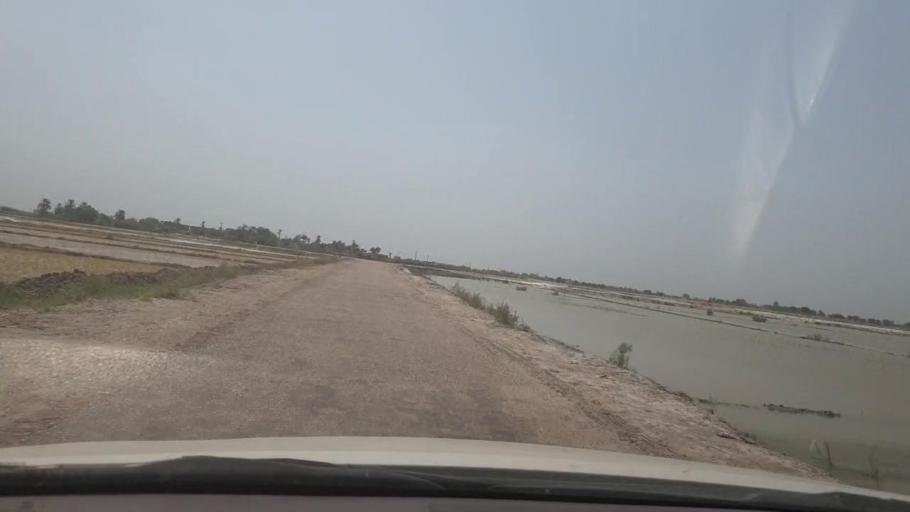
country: PK
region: Sindh
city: Shikarpur
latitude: 27.9926
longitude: 68.5673
